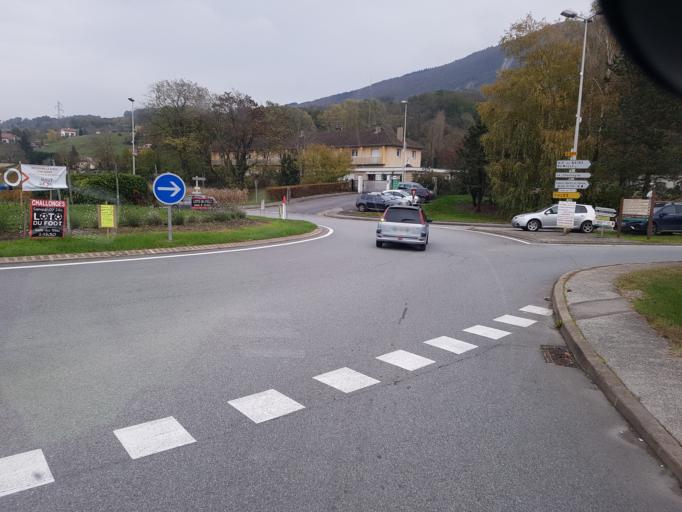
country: FR
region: Rhone-Alpes
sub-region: Departement de la Haute-Savoie
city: Versonnex
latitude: 45.9538
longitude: 5.8373
